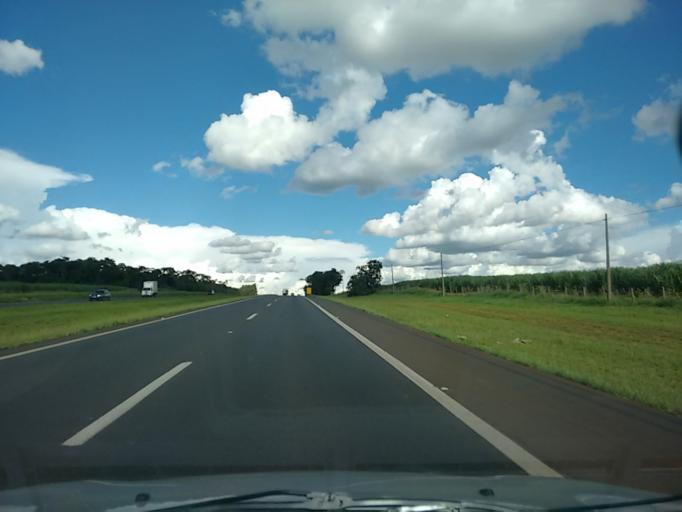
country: BR
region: Sao Paulo
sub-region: Ibate
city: Ibate
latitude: -21.9692
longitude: -47.9559
